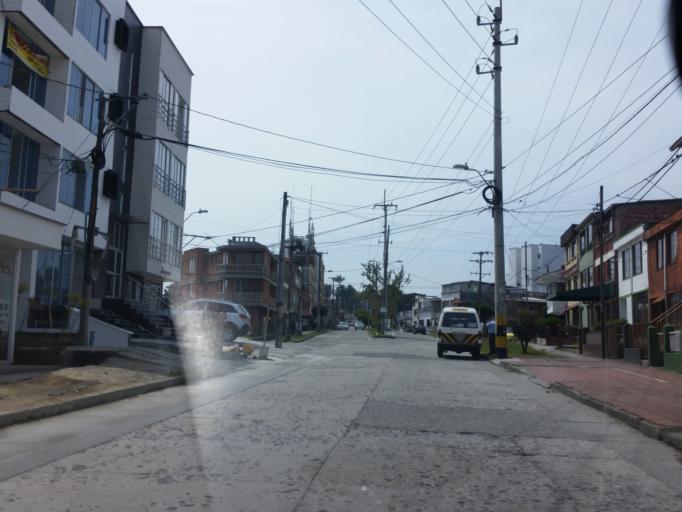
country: CO
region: Caldas
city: Manizales
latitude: 5.0761
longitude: -75.5240
